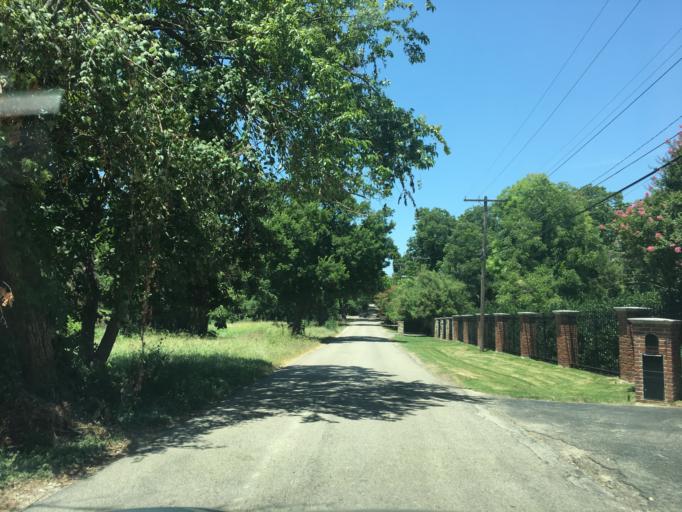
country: US
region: Texas
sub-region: Dallas County
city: Highland Park
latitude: 32.8370
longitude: -96.7305
